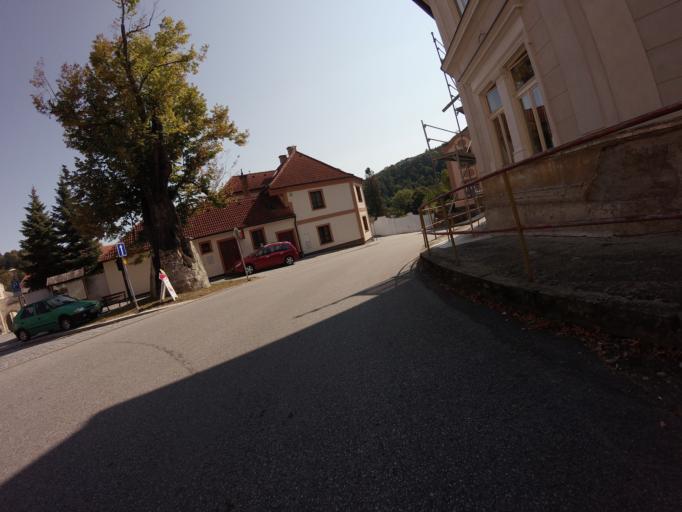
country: CZ
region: Jihocesky
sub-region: Okres Cesky Krumlov
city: Cesky Krumlov
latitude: 48.8548
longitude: 14.3695
